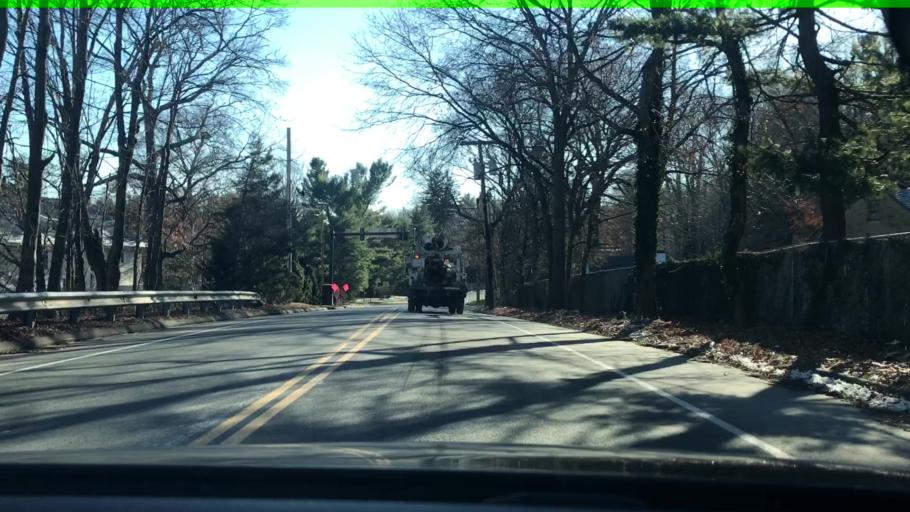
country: US
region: Connecticut
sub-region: New Haven County
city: New Haven
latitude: 41.3210
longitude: -72.9701
